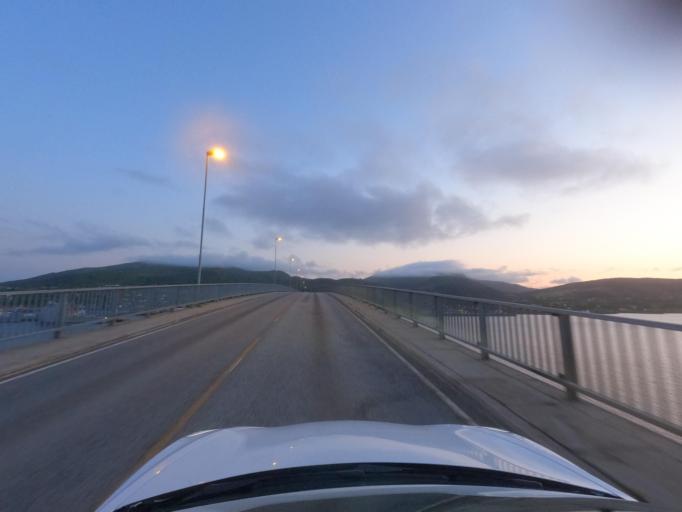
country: NO
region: Nordland
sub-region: Sortland
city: Sortland
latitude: 68.7066
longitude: 15.4299
